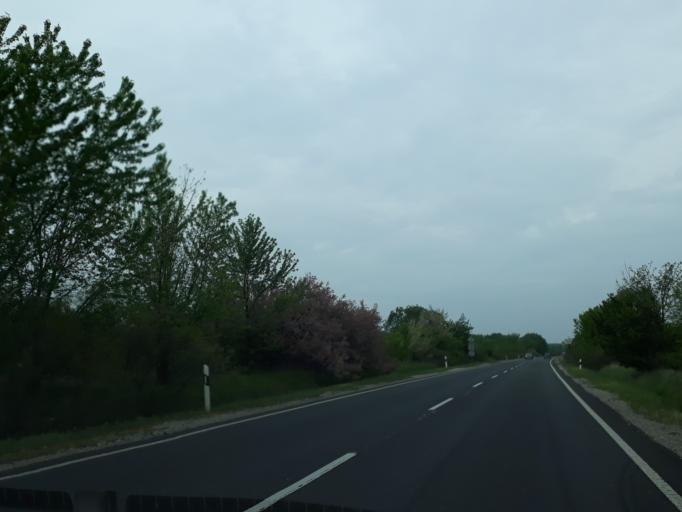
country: HU
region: Szabolcs-Szatmar-Bereg
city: Demecser
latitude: 48.0696
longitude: 21.9489
